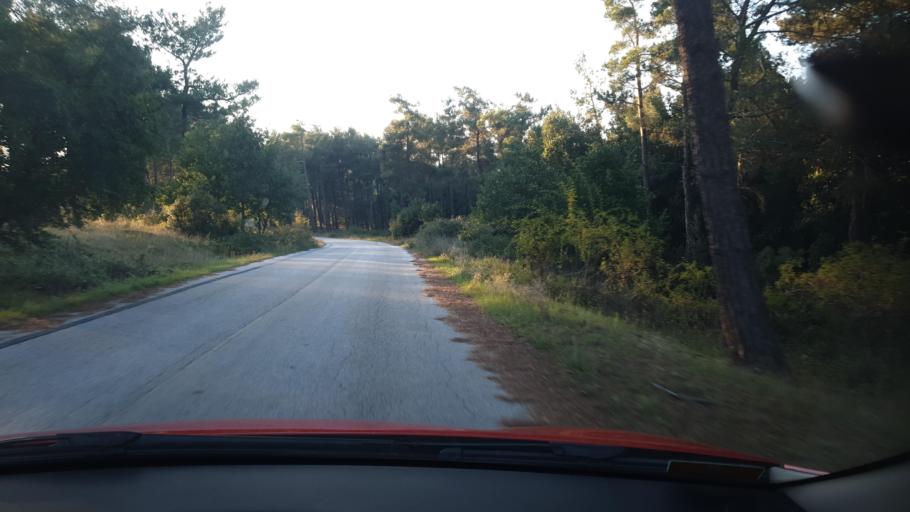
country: GR
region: Central Macedonia
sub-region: Nomos Thessalonikis
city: Peristera
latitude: 40.5120
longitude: 23.2173
